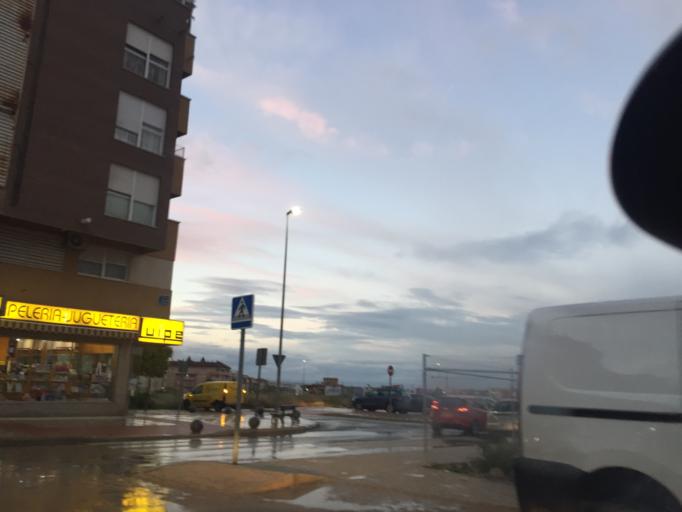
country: ES
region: Andalusia
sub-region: Provincia de Jaen
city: Jaen
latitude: 37.7829
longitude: -3.7876
